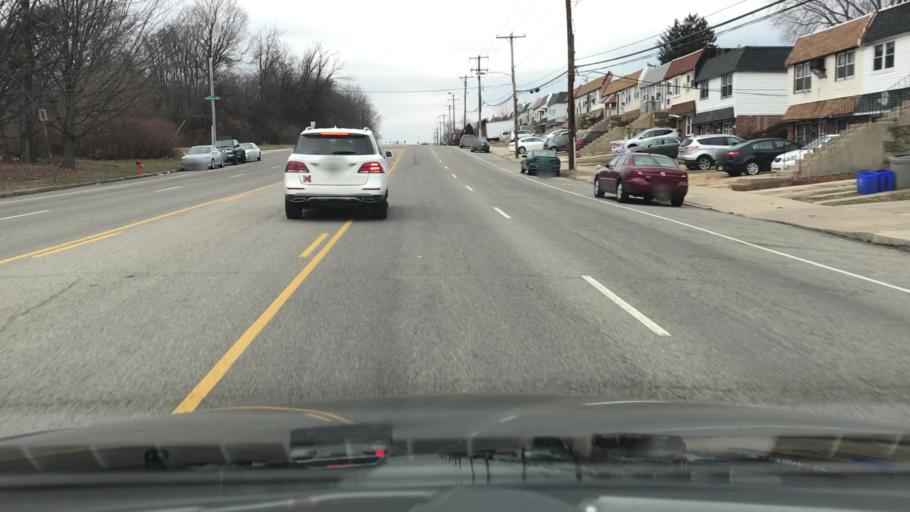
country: US
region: Pennsylvania
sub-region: Bucks County
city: Cornwells Heights
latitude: 40.0912
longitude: -74.9857
